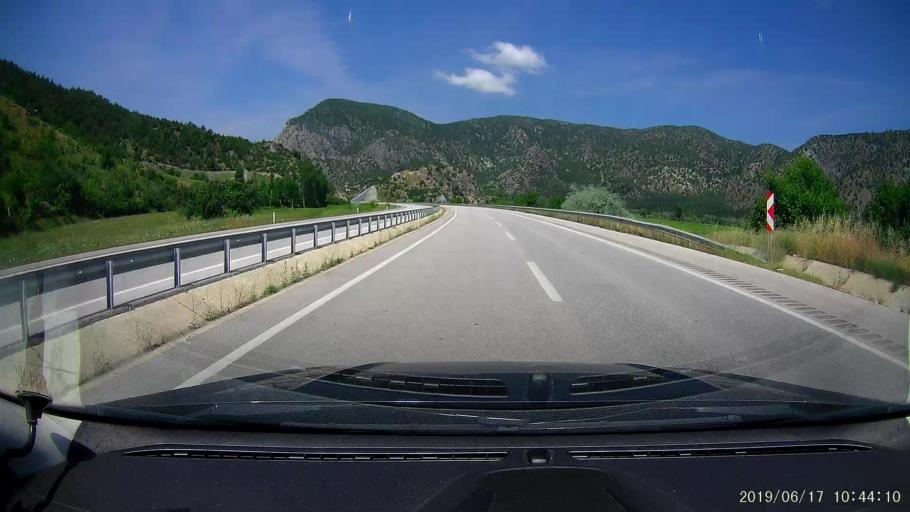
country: TR
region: Corum
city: Kargi
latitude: 41.0719
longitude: 34.5195
